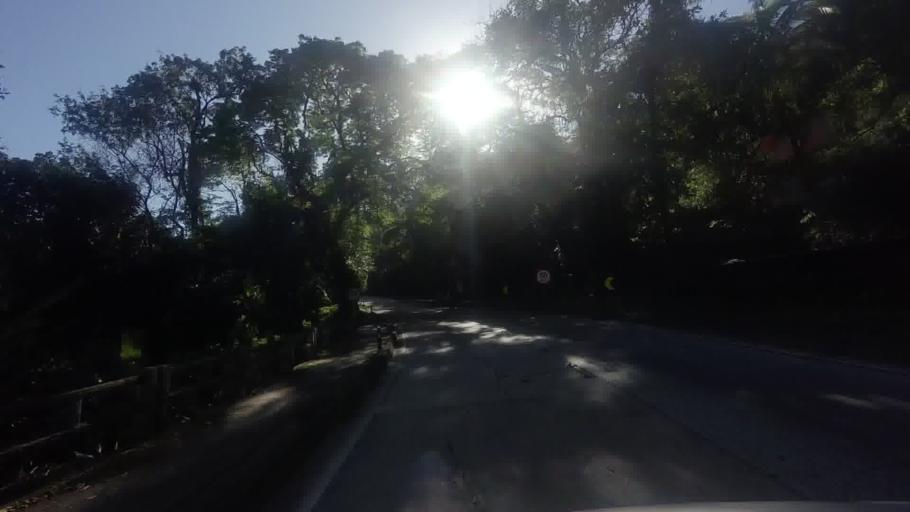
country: BR
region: Rio de Janeiro
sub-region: Petropolis
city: Petropolis
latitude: -22.5875
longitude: -43.2674
